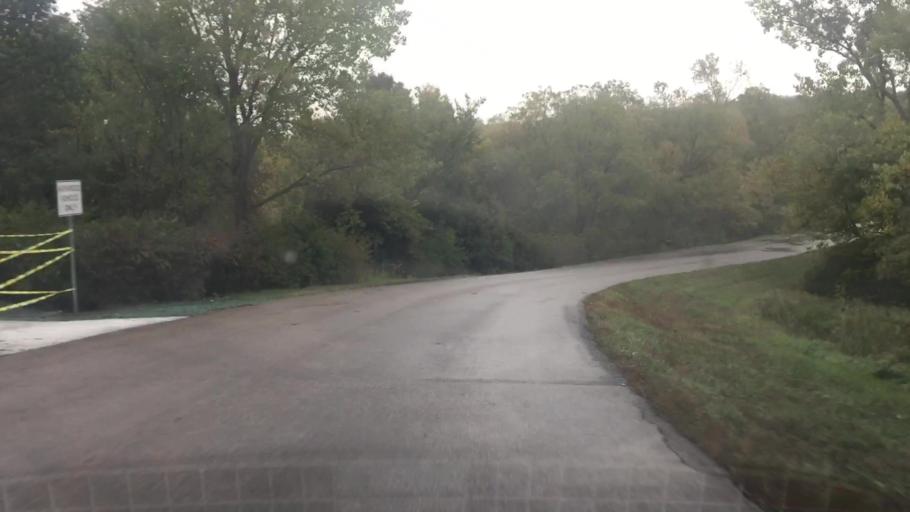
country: US
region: Kansas
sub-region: Johnson County
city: Lenexa
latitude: 38.9759
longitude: -94.8039
